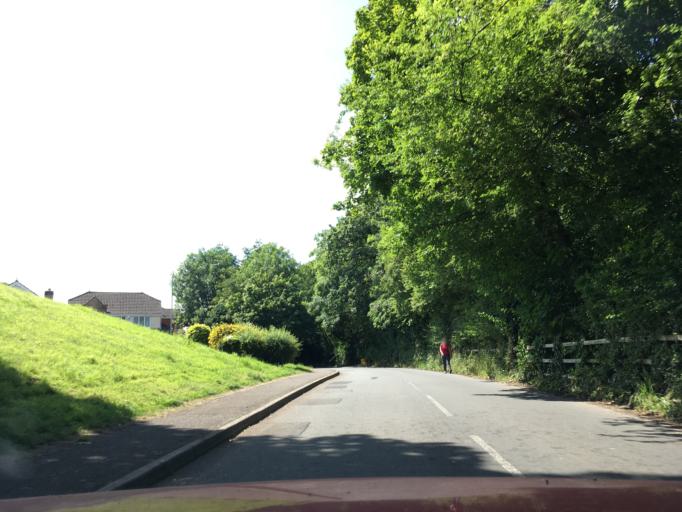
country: GB
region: Wales
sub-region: Newport
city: Newport
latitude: 51.5931
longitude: -3.0135
